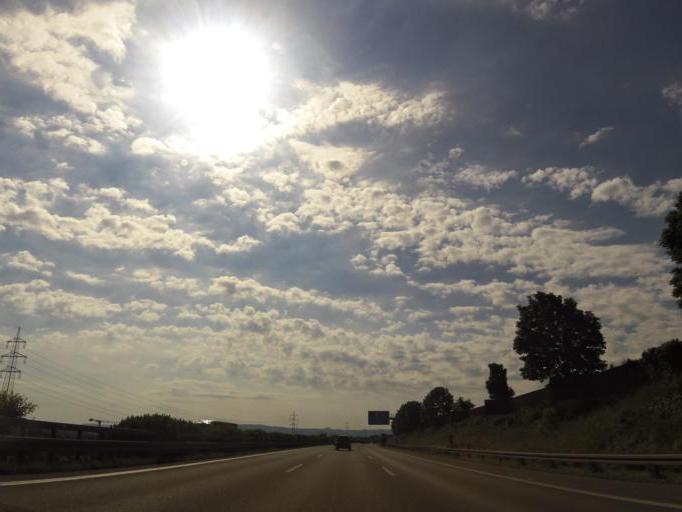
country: DE
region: Baden-Wuerttemberg
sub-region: Regierungsbezirk Stuttgart
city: Kirchheim unter Teck
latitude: 48.6483
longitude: 9.4169
